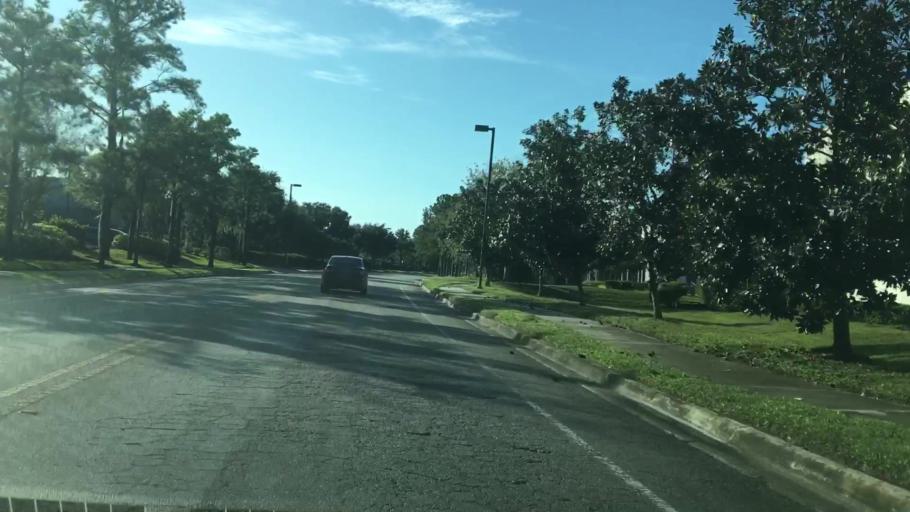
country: US
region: Florida
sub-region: Orange County
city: Conway
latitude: 28.4631
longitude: -81.2965
